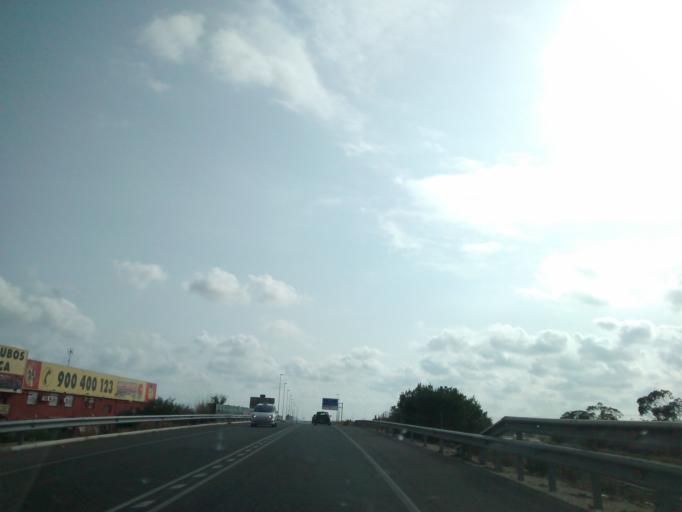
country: ES
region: Valencia
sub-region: Provincia de Alicante
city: el Campello
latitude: 38.4478
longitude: -0.3831
